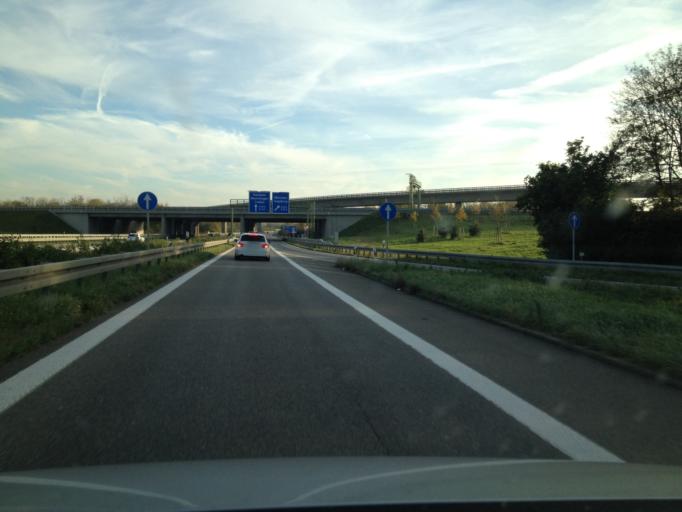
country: DE
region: Baden-Wuerttemberg
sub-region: Tuebingen Region
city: Langenau
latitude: 48.4668
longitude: 10.1146
